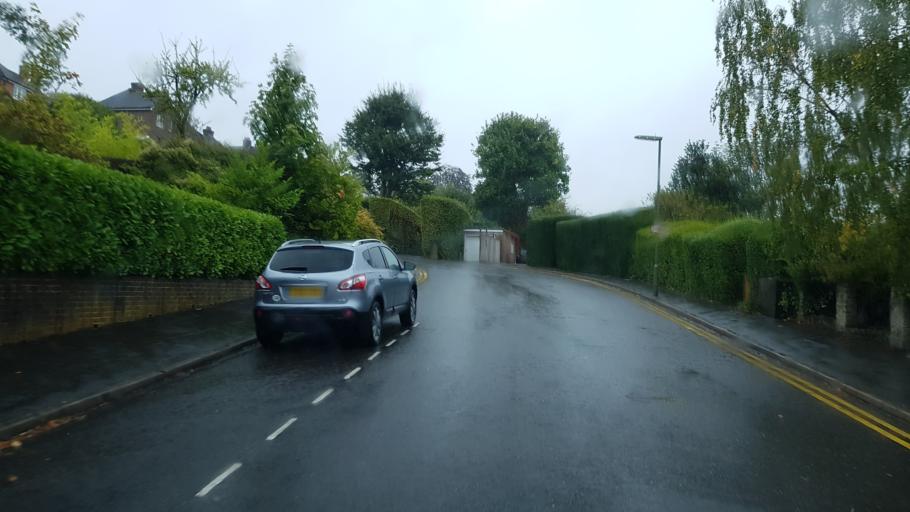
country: GB
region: England
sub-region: Surrey
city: Guildford
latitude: 51.2328
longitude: -0.5831
